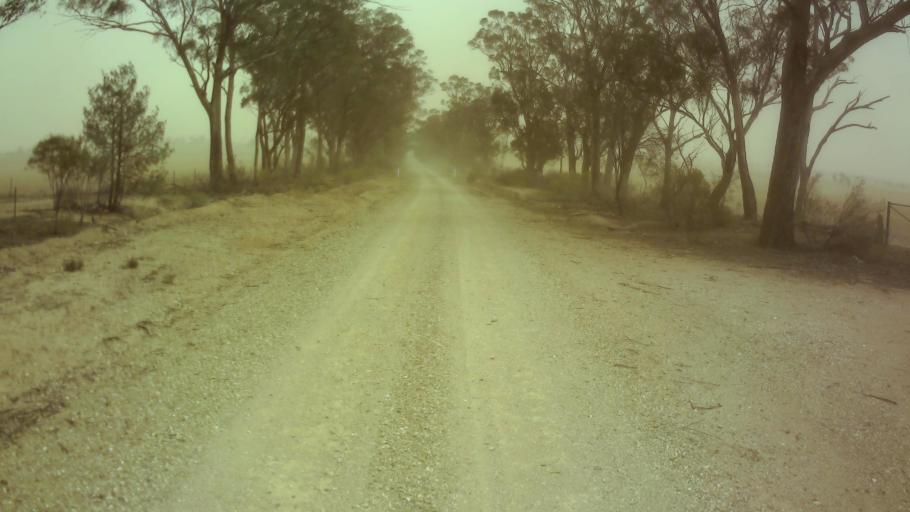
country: AU
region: New South Wales
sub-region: Weddin
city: Grenfell
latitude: -33.7087
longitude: 147.9440
